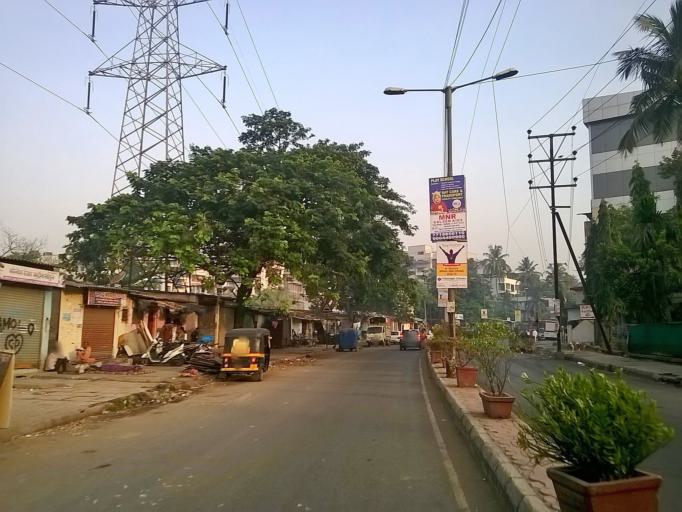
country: IN
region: Maharashtra
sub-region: Raigarh
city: Panvel
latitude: 18.9938
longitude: 73.1203
